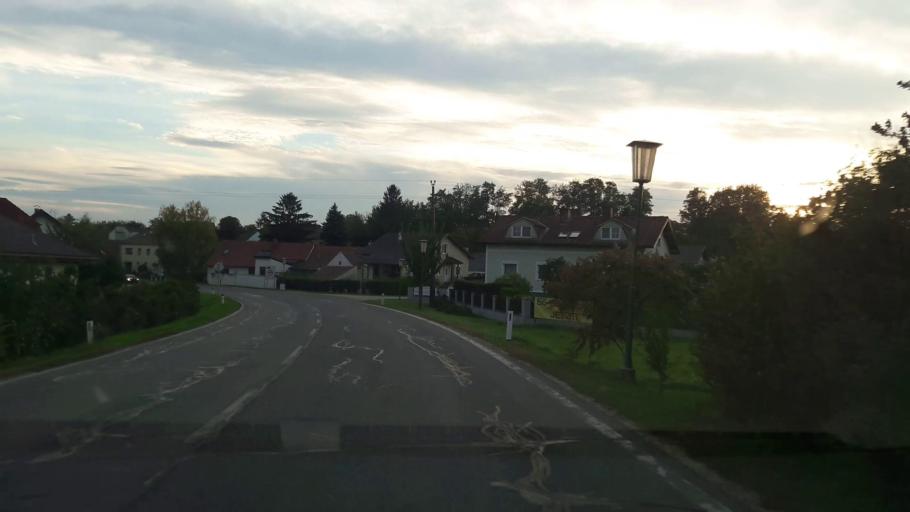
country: AT
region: Lower Austria
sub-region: Politischer Bezirk Korneuburg
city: Harmannsdorf
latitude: 48.4002
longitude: 16.3732
